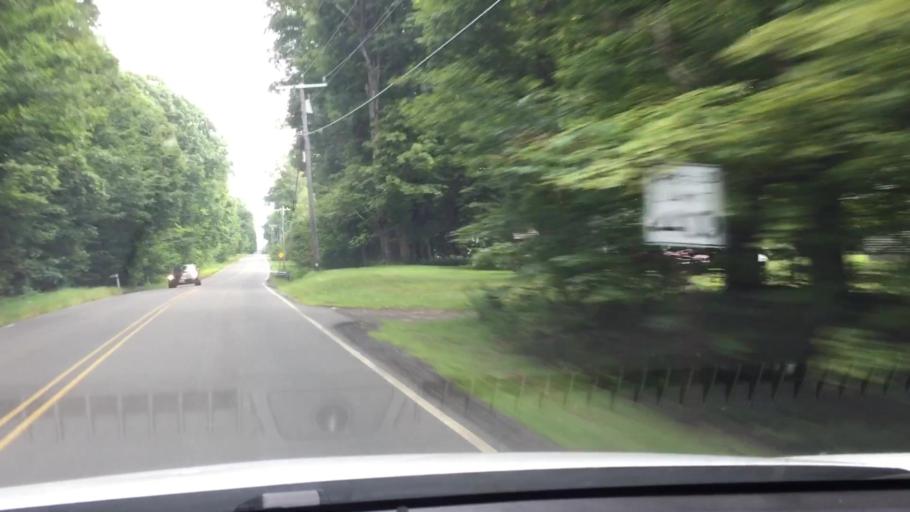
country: US
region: Massachusetts
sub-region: Berkshire County
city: Otis
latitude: 42.2107
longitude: -72.9428
